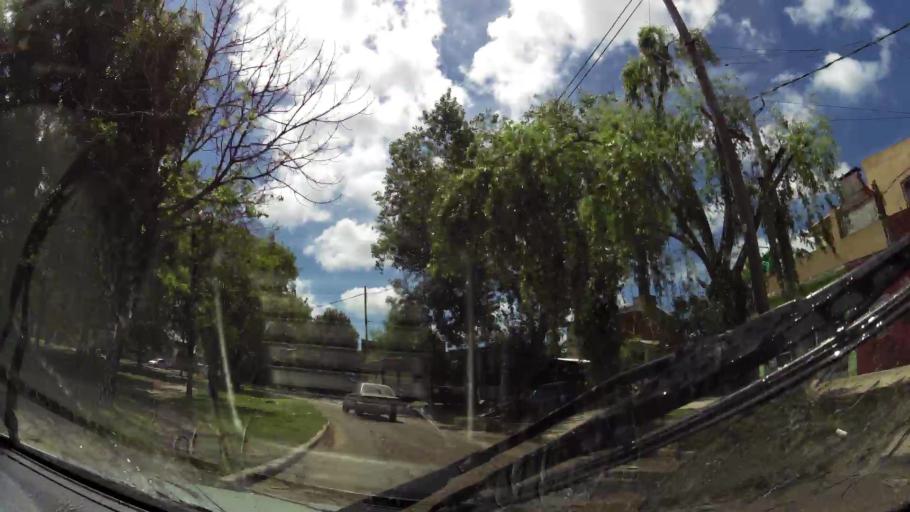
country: AR
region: Buenos Aires
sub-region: Partido de Quilmes
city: Quilmes
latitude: -34.8253
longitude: -58.2326
